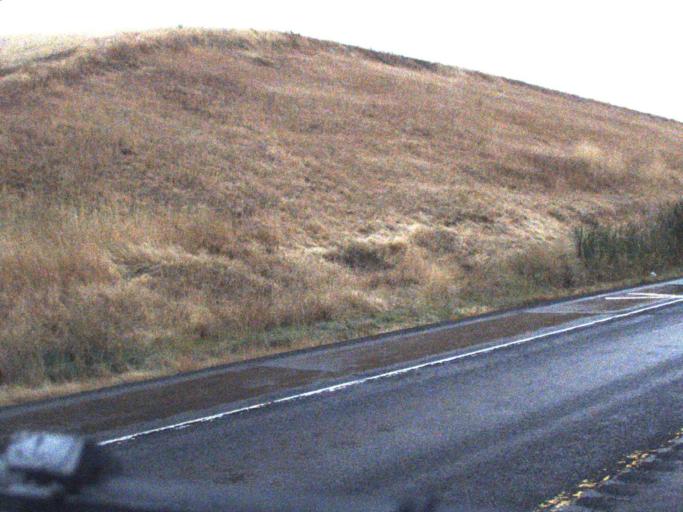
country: US
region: Washington
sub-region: Spokane County
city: Cheney
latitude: 47.2352
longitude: -117.3603
